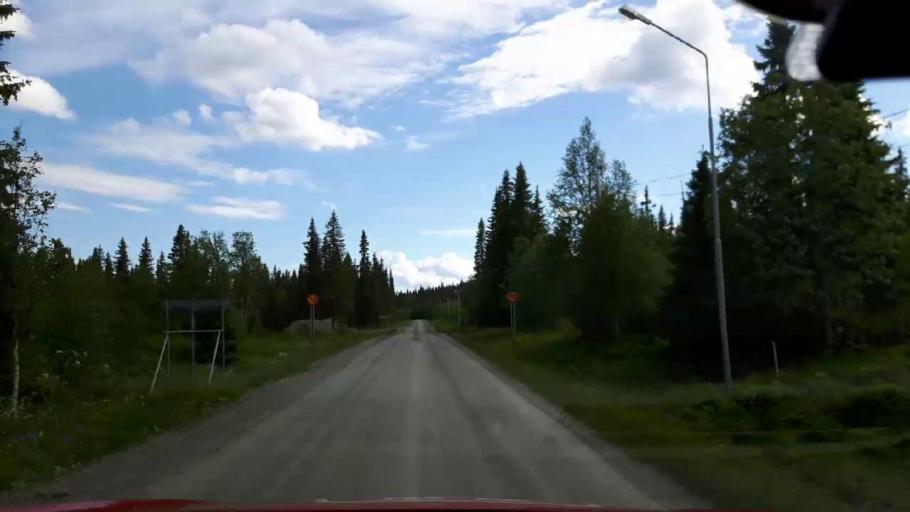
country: SE
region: Jaemtland
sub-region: Krokoms Kommun
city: Valla
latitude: 63.8243
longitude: 14.0408
